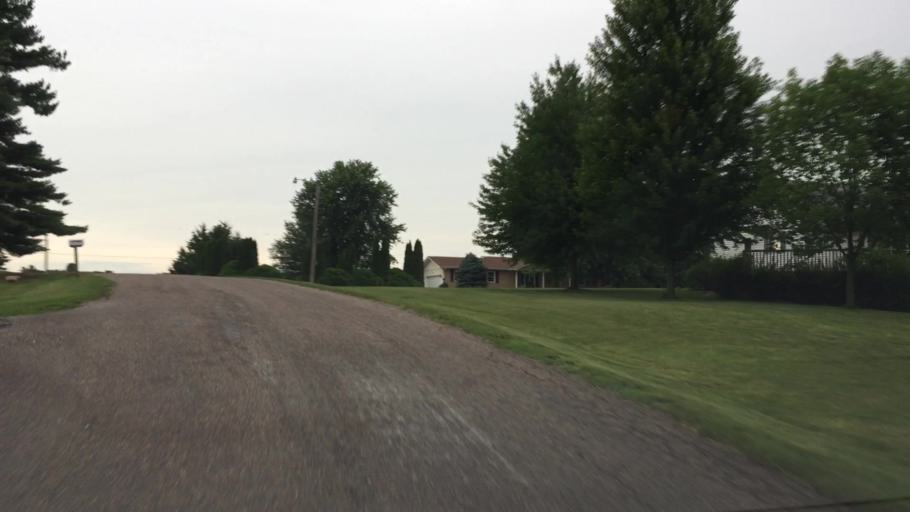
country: US
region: Illinois
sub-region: Hancock County
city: Nauvoo
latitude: 40.5319
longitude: -91.3704
